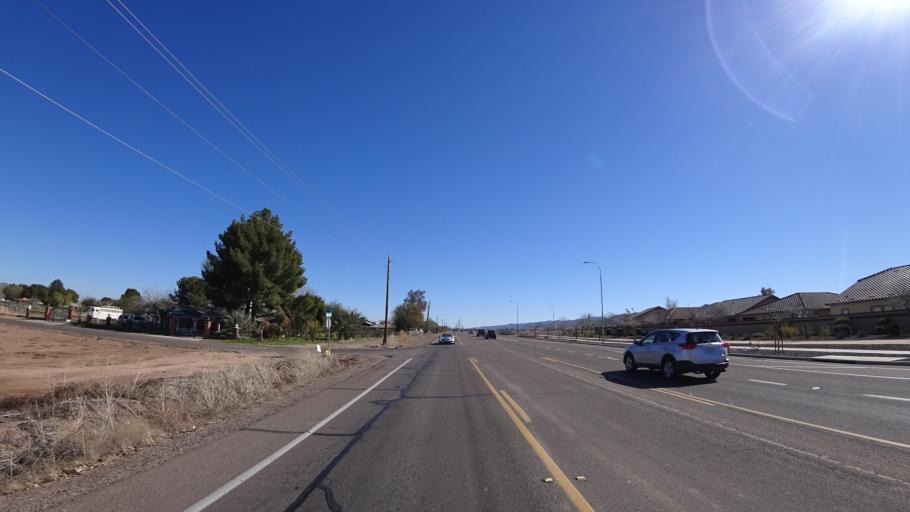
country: US
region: Arizona
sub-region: Maricopa County
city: Laveen
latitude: 33.3774
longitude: -112.1960
